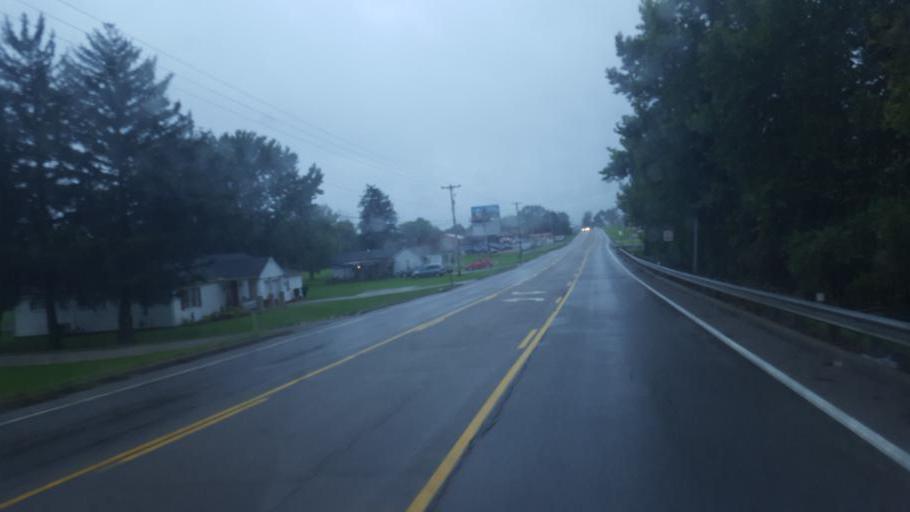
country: US
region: Ohio
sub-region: Jackson County
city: Jackson
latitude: 39.0300
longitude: -82.6236
